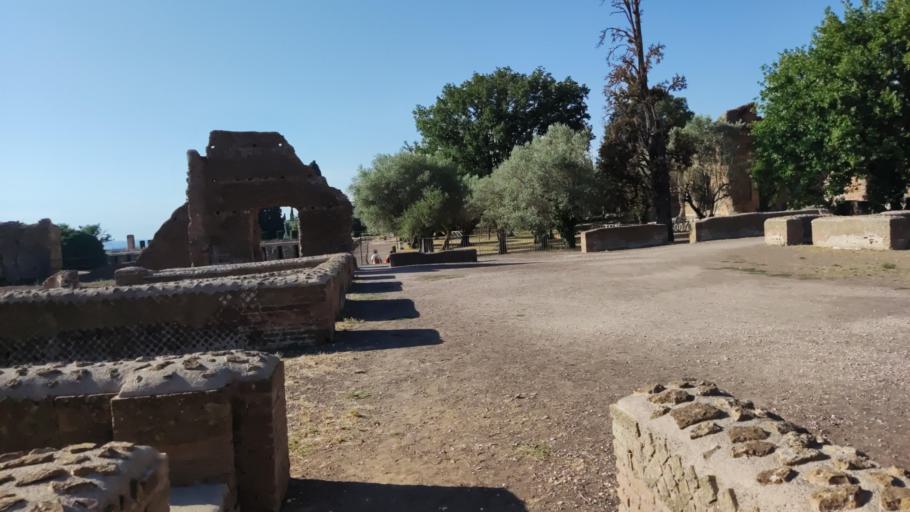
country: IT
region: Latium
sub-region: Citta metropolitana di Roma Capitale
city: Villa Adriana
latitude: 41.9399
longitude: 12.7750
